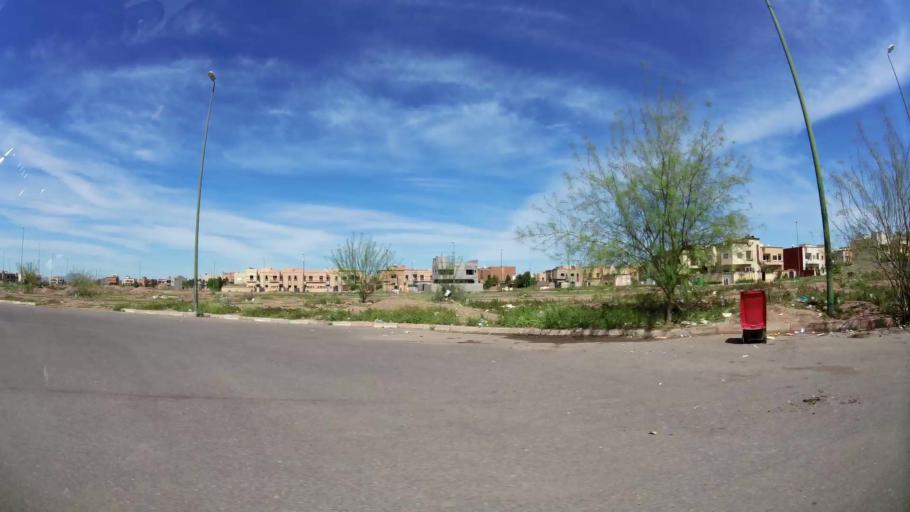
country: MA
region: Marrakech-Tensift-Al Haouz
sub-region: Marrakech
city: Marrakesh
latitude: 31.6492
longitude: -8.0749
